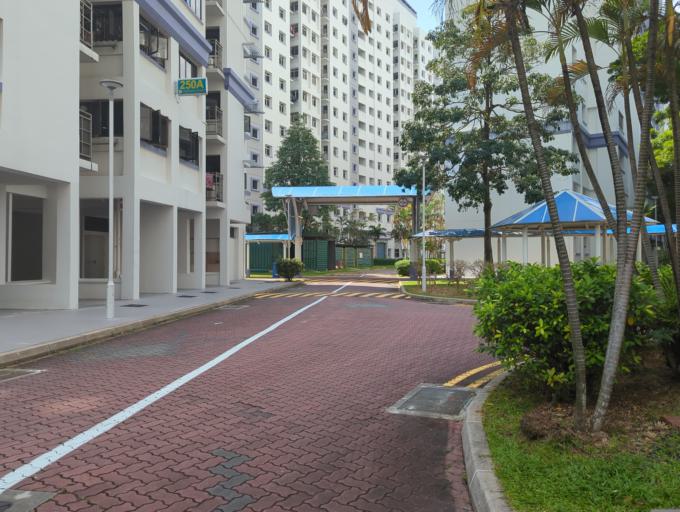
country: MY
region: Johor
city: Kampung Pasir Gudang Baru
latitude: 1.3920
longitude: 103.8999
